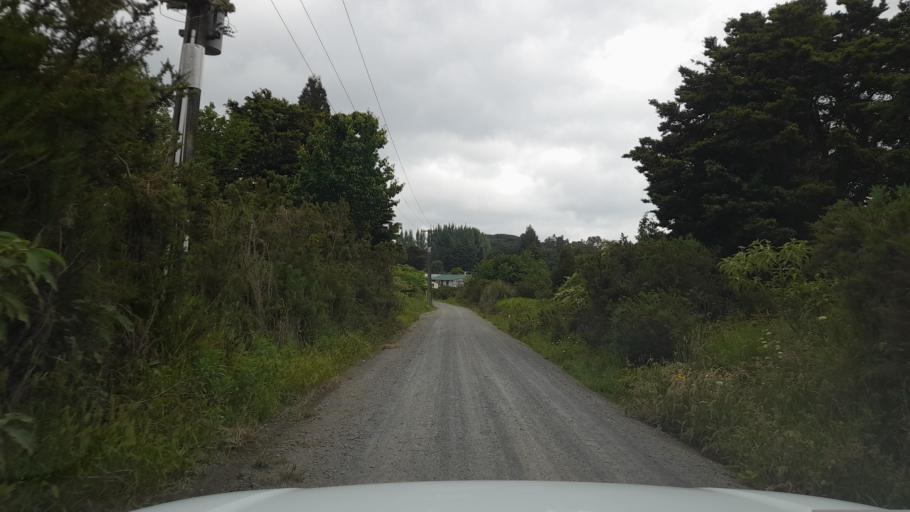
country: NZ
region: Northland
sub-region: Far North District
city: Waimate North
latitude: -35.4009
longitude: 173.7862
